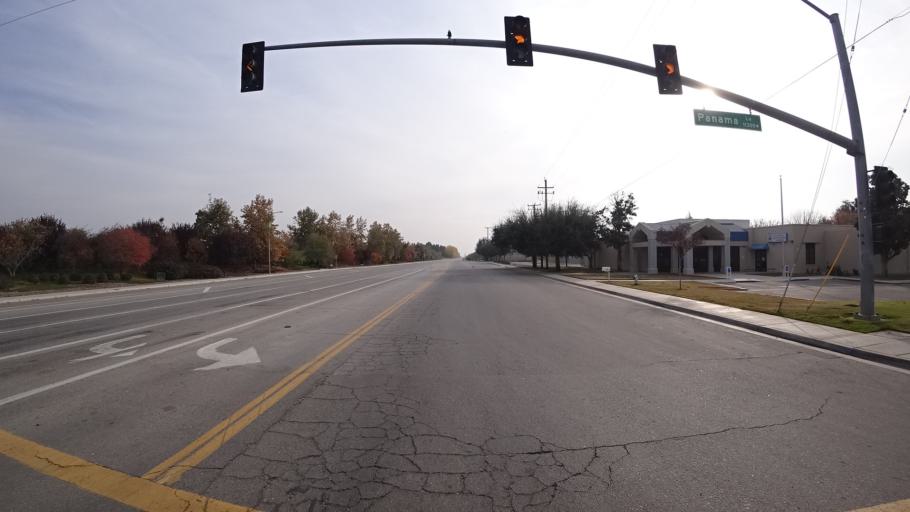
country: US
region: California
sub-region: Kern County
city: Greenacres
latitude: 35.2961
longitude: -119.1282
